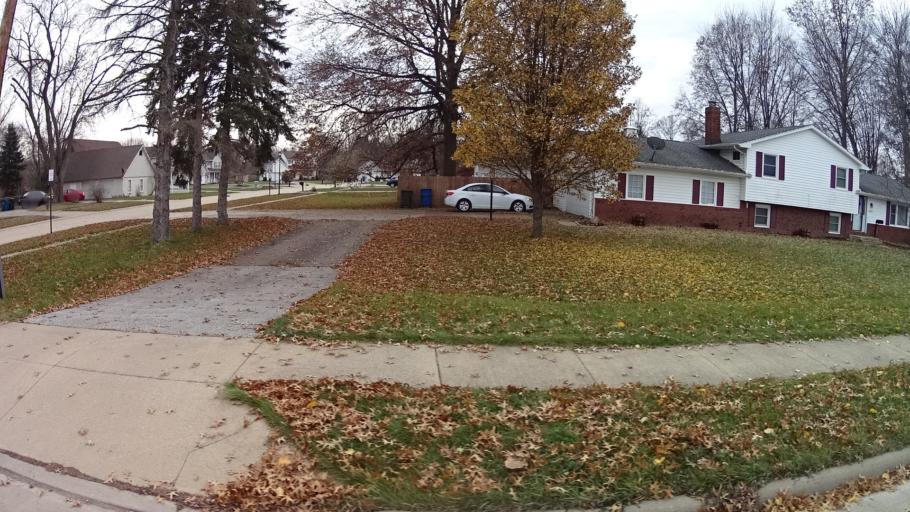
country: US
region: Ohio
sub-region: Lorain County
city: North Ridgeville
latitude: 41.3852
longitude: -82.0023
